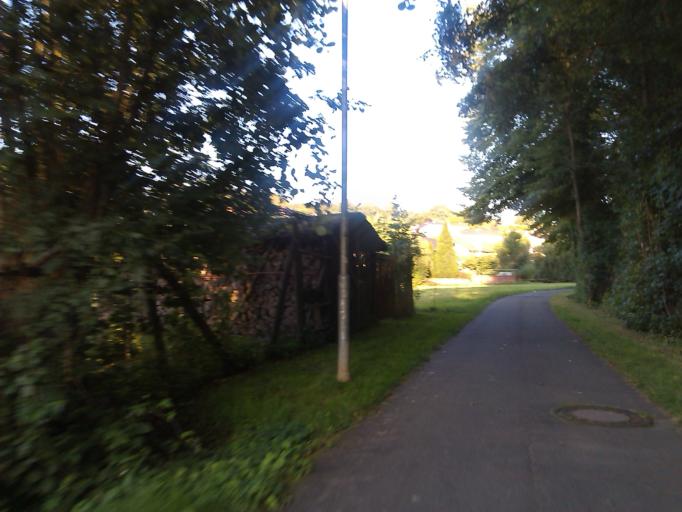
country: DE
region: Baden-Wuerttemberg
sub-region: Karlsruhe Region
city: Balzfeld
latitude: 49.2382
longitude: 8.7725
